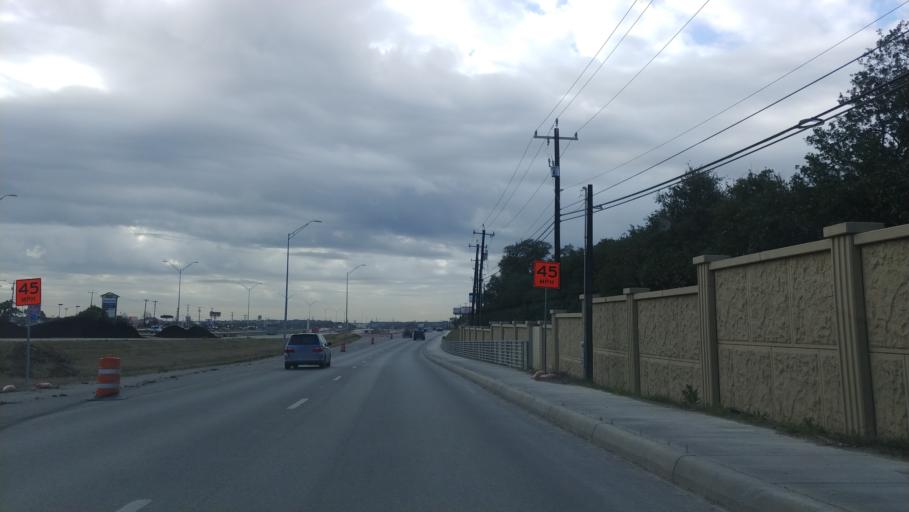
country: US
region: Texas
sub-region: Bexar County
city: Leon Valley
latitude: 29.4419
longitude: -98.7116
